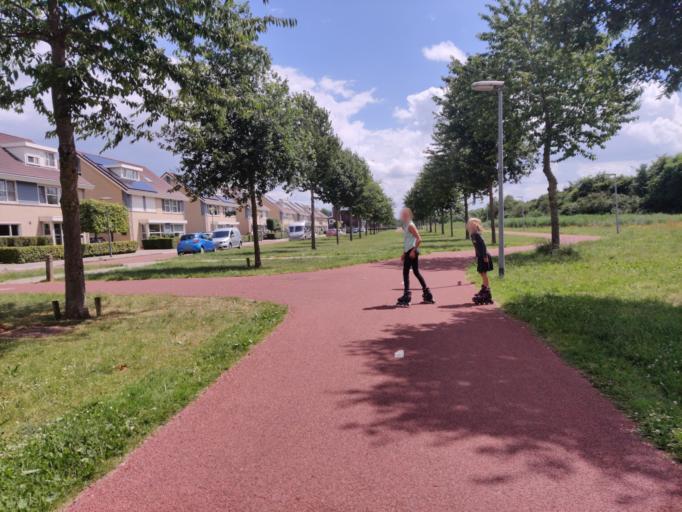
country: NL
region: Flevoland
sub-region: Gemeente Zeewolde
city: Zeewolde
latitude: 52.3434
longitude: 5.5212
